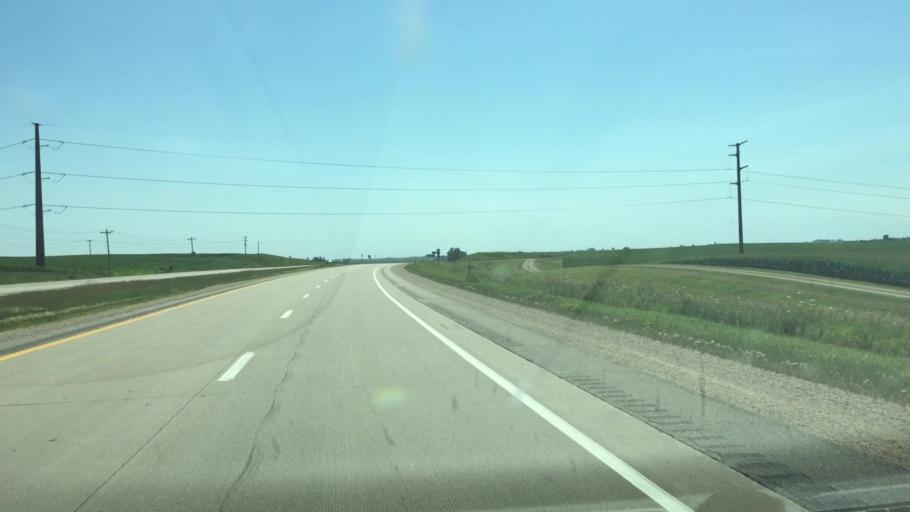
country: US
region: Iowa
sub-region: Dubuque County
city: Peosta
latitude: 42.3651
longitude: -90.7994
